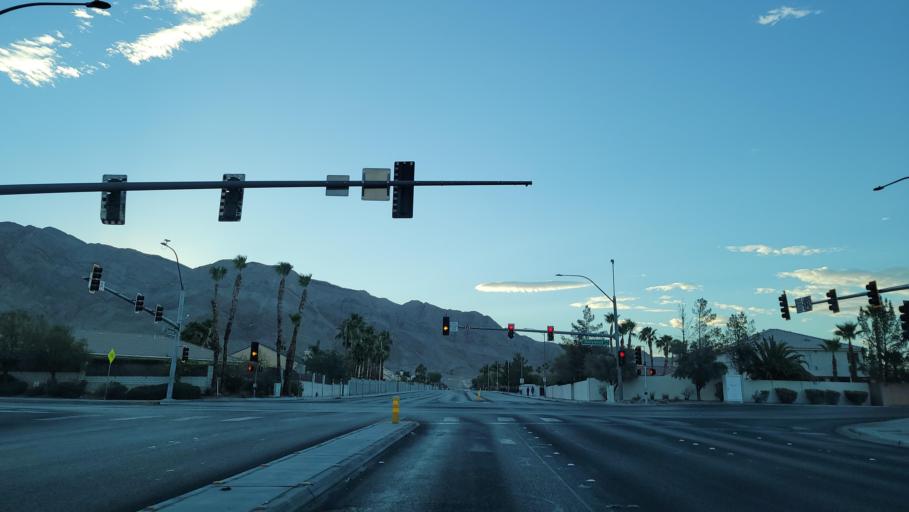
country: US
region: Nevada
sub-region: Clark County
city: Sunrise Manor
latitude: 36.1592
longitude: -115.0264
